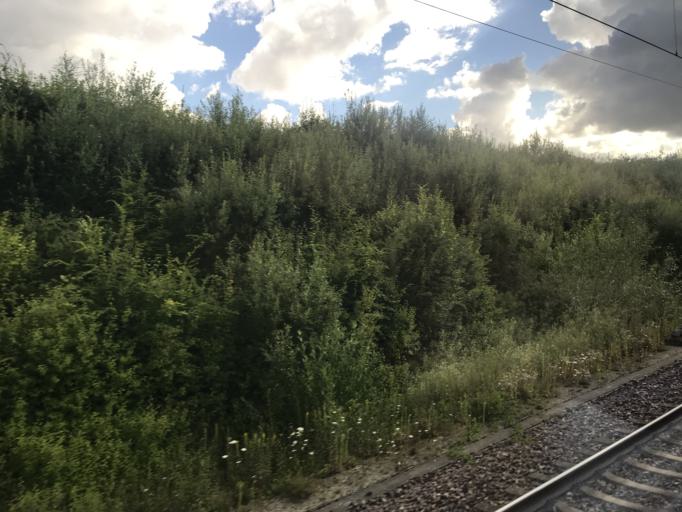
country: LU
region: Luxembourg
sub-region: Canton d'Esch-sur-Alzette
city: Petange
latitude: 49.5560
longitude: 5.8907
